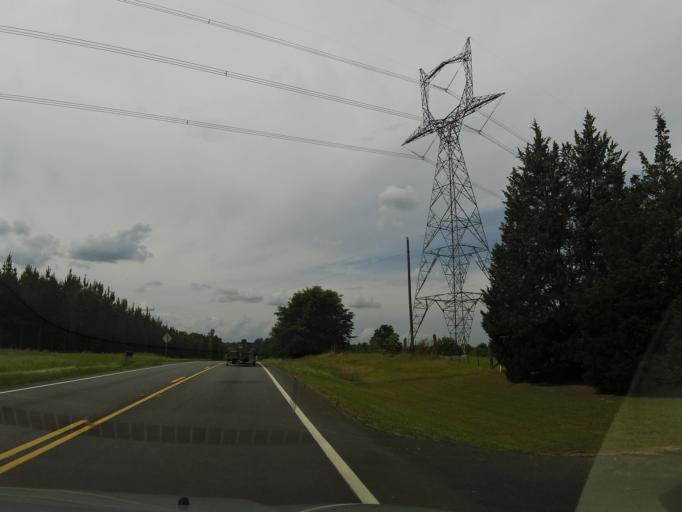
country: US
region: Georgia
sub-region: McDuffie County
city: Thomson
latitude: 33.3706
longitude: -82.4678
